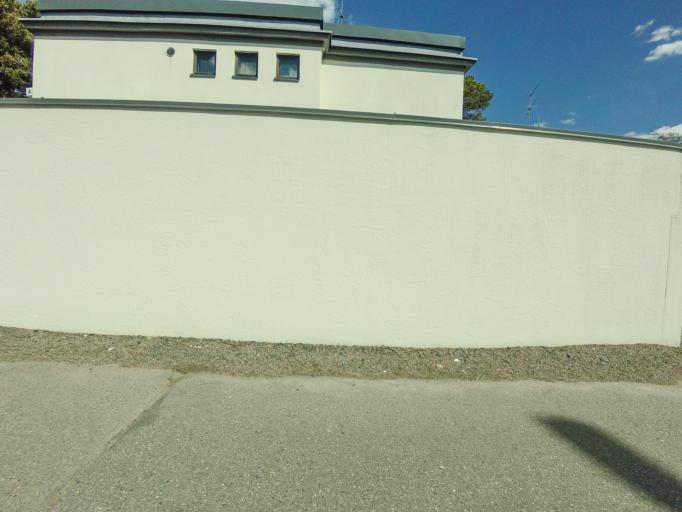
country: FI
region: Uusimaa
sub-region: Helsinki
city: Helsinki
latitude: 60.1587
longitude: 25.0496
